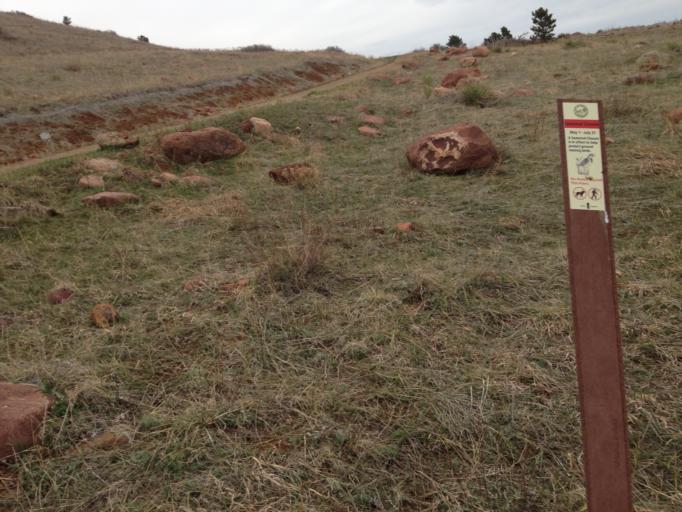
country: US
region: Colorado
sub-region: Boulder County
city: Boulder
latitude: 39.9454
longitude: -105.2632
